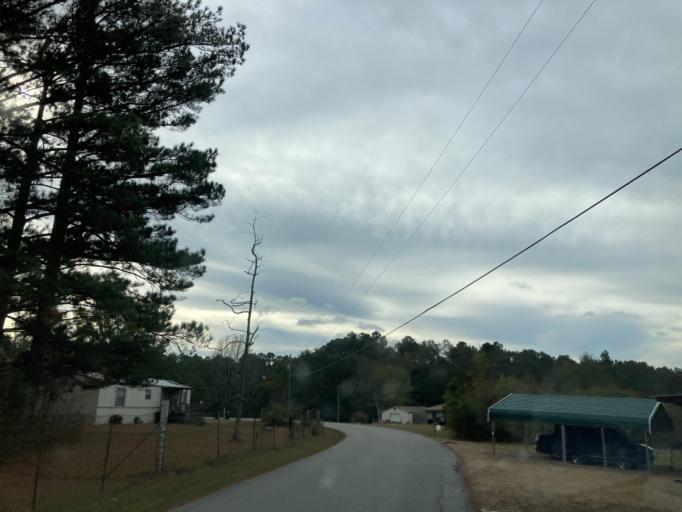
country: US
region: Mississippi
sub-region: Lamar County
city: Purvis
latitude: 31.1595
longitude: -89.4598
